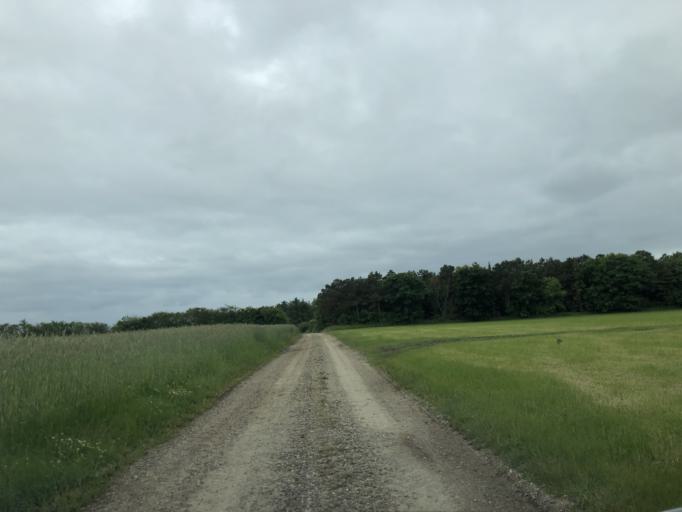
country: DK
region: Central Jutland
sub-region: Holstebro Kommune
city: Ulfborg
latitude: 56.2281
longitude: 8.1735
